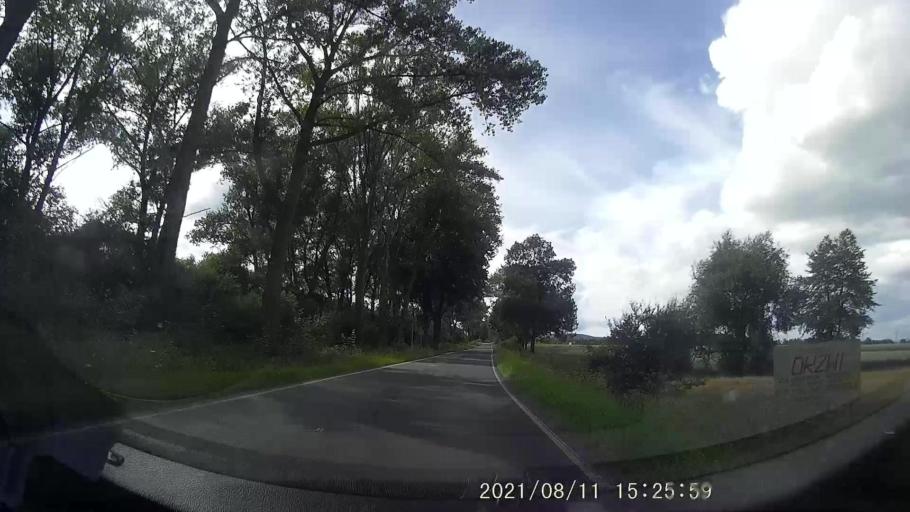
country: PL
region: Lower Silesian Voivodeship
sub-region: Powiat klodzki
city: Bystrzyca Klodzka
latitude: 50.2907
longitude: 16.6682
